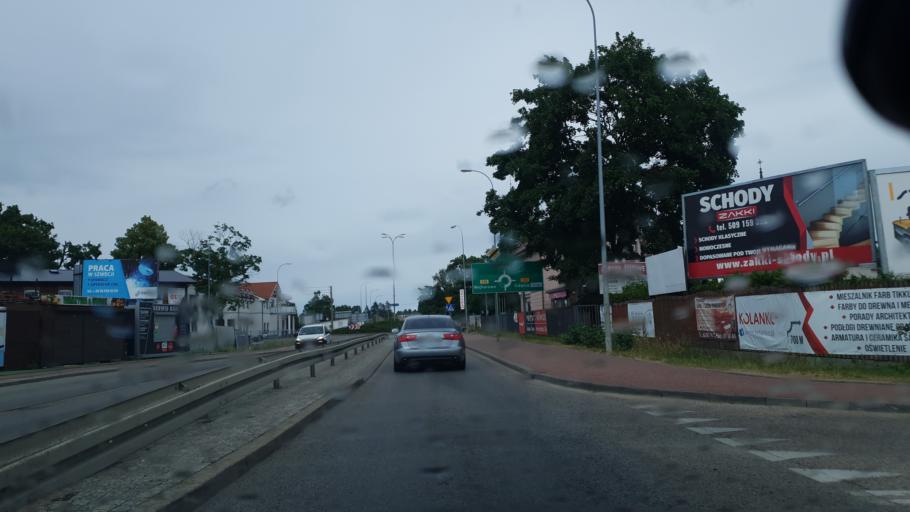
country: PL
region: Pomeranian Voivodeship
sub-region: Powiat kartuski
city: Chwaszczyno
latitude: 54.4428
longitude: 18.4180
